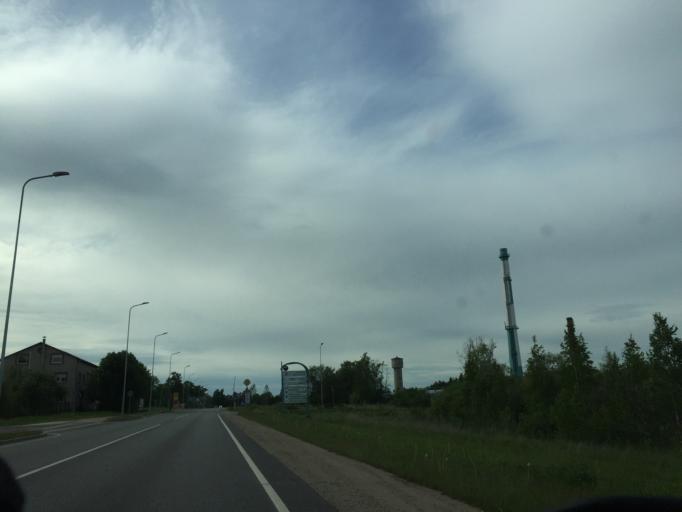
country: LV
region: Valmieras Rajons
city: Valmiera
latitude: 57.5202
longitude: 25.4538
